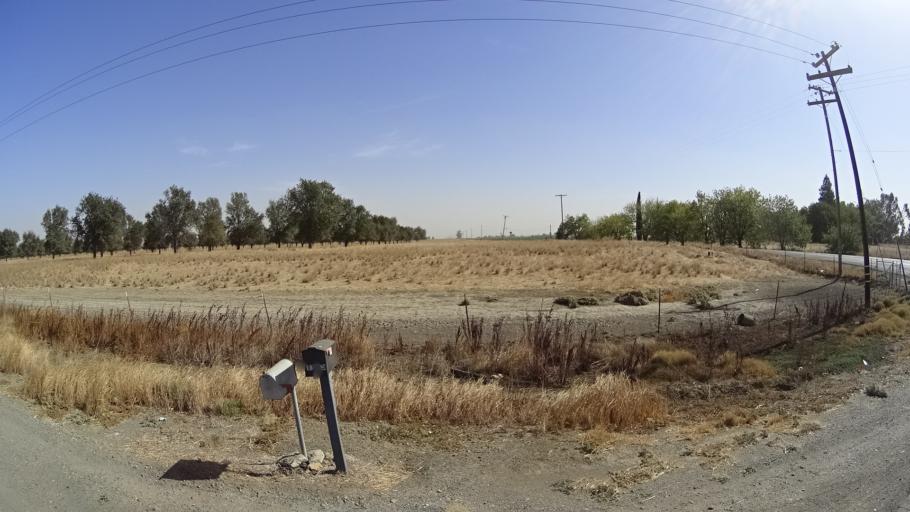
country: US
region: California
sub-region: Yolo County
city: Davis
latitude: 38.4879
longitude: -121.6958
